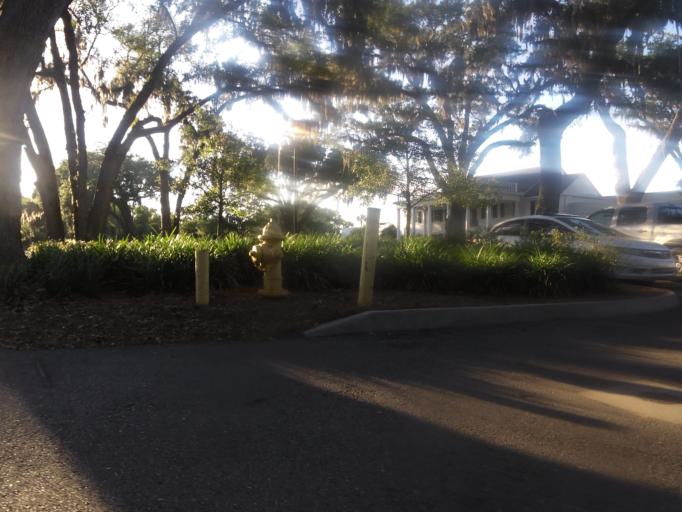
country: US
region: Florida
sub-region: Clay County
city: Orange Park
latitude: 30.2465
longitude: -81.6853
